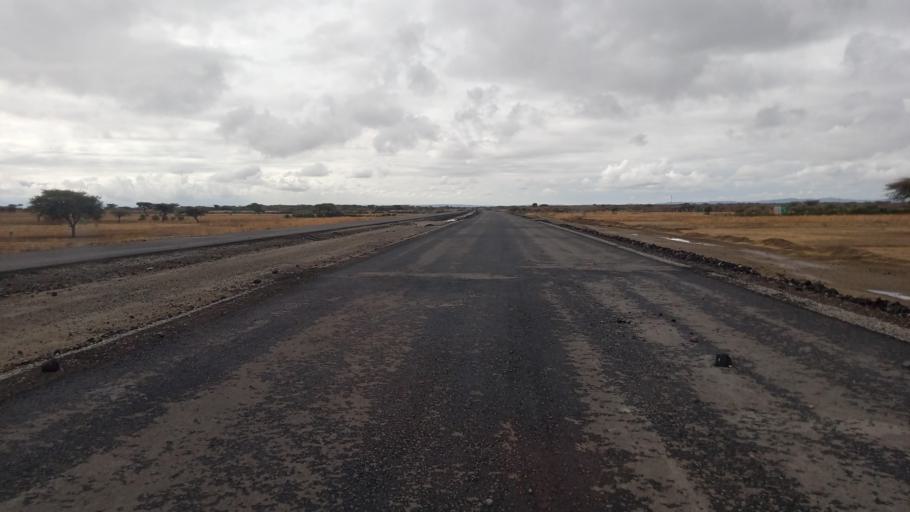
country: ET
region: Oromiya
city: Ziway
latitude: 7.6281
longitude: 38.6799
